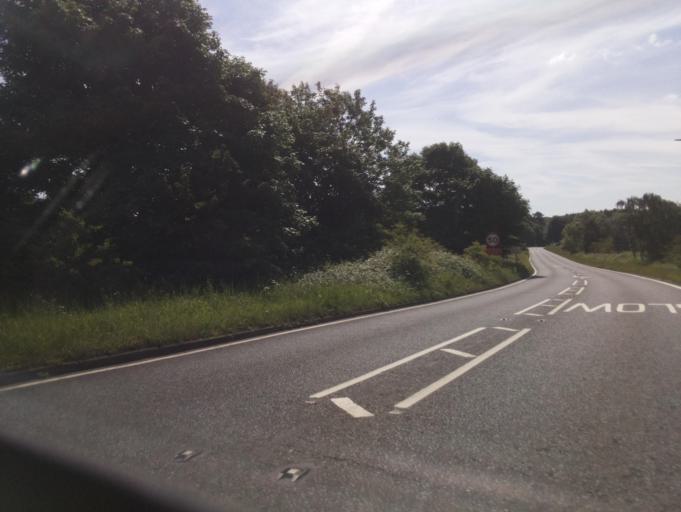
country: GB
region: England
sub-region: North Lincolnshire
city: Broughton
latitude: 53.5545
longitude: -0.5845
